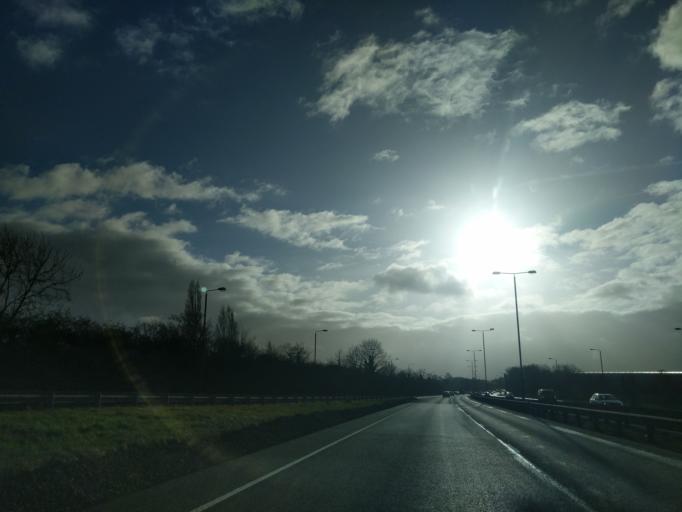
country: GB
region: England
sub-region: Derbyshire
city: Findern
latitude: 52.8833
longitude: -1.5468
